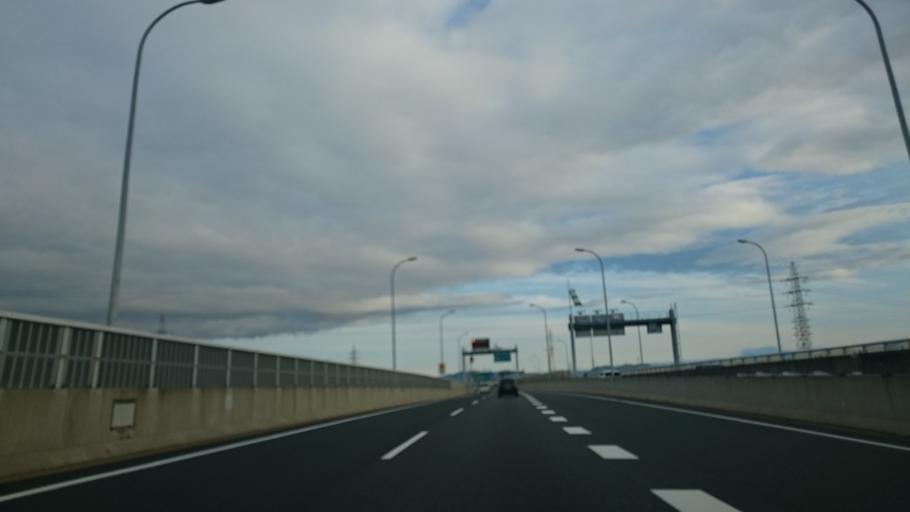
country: JP
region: Aichi
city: Komaki
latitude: 35.2923
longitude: 136.9058
